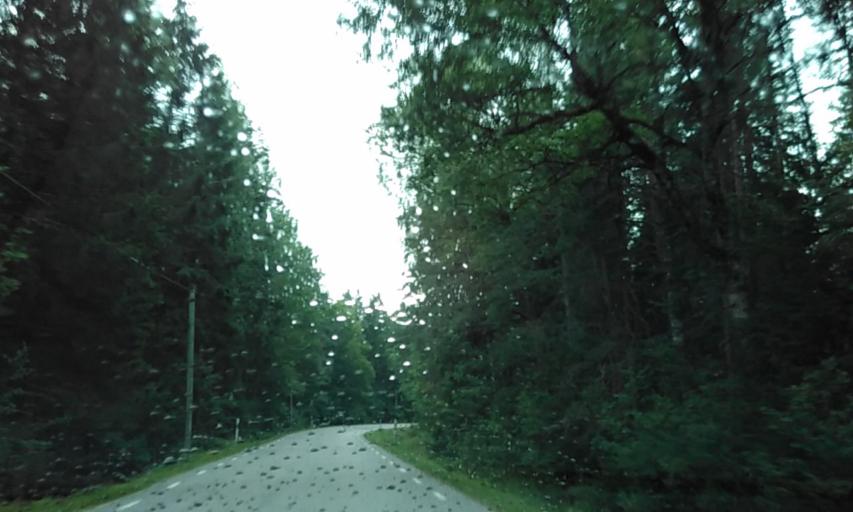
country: SE
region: Vaestra Goetaland
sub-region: Grastorps Kommun
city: Graestorp
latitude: 58.4563
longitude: 12.7954
